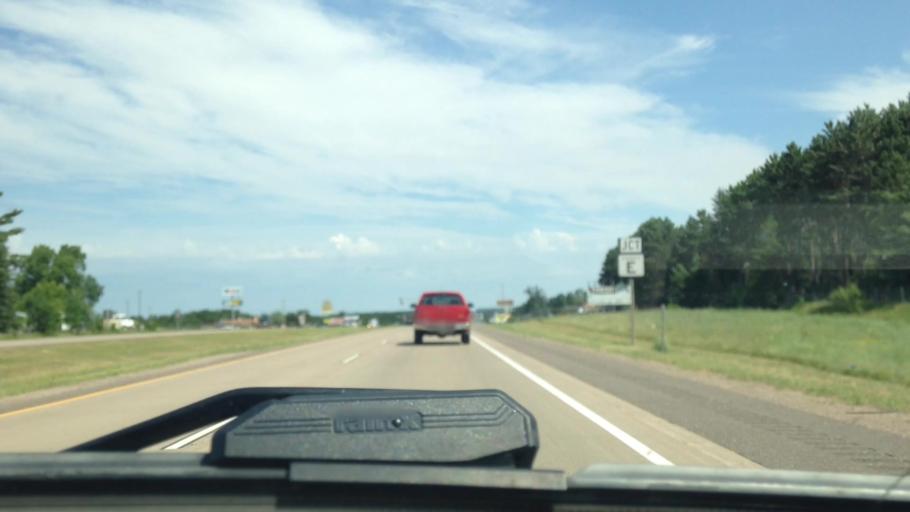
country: US
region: Wisconsin
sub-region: Washburn County
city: Spooner
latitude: 45.8966
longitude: -91.8276
